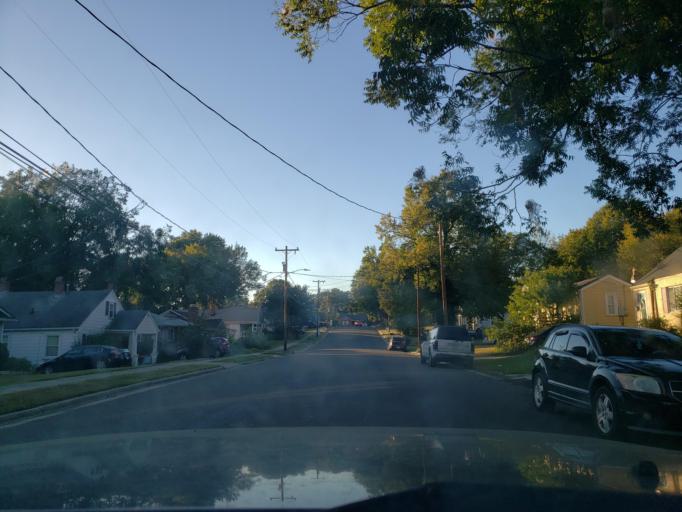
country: US
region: North Carolina
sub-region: Durham County
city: Durham
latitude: 35.9648
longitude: -78.9038
